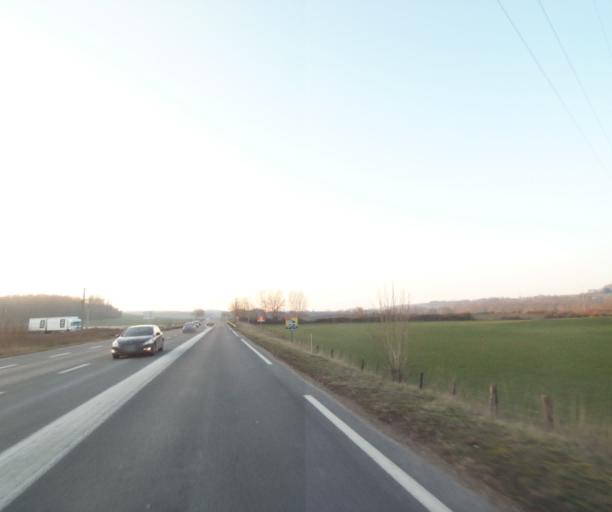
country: FR
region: Lorraine
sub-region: Departement de la Meuse
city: Ancerville
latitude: 48.6055
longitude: 5.0260
